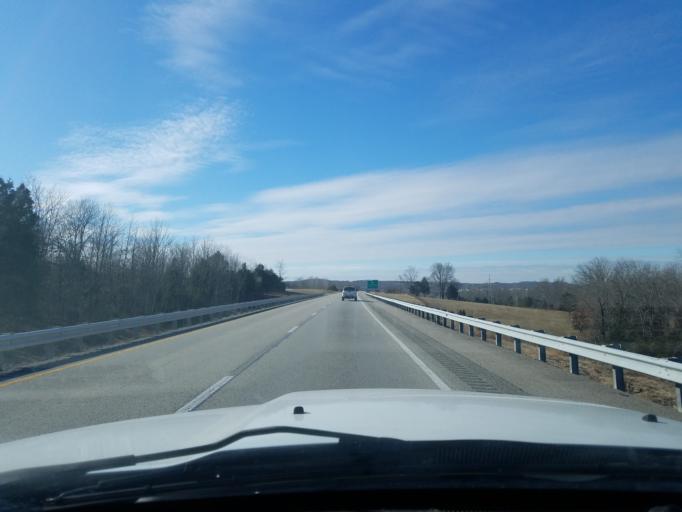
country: US
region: Kentucky
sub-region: Grayson County
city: Leitchfield
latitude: 37.4686
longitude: -86.2712
